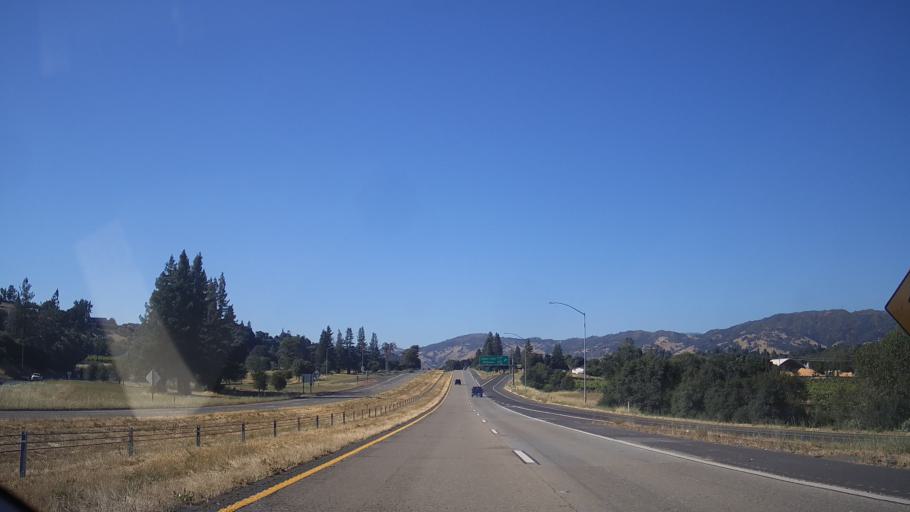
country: US
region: California
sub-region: Mendocino County
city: Redwood Valley
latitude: 39.2355
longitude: -123.2080
